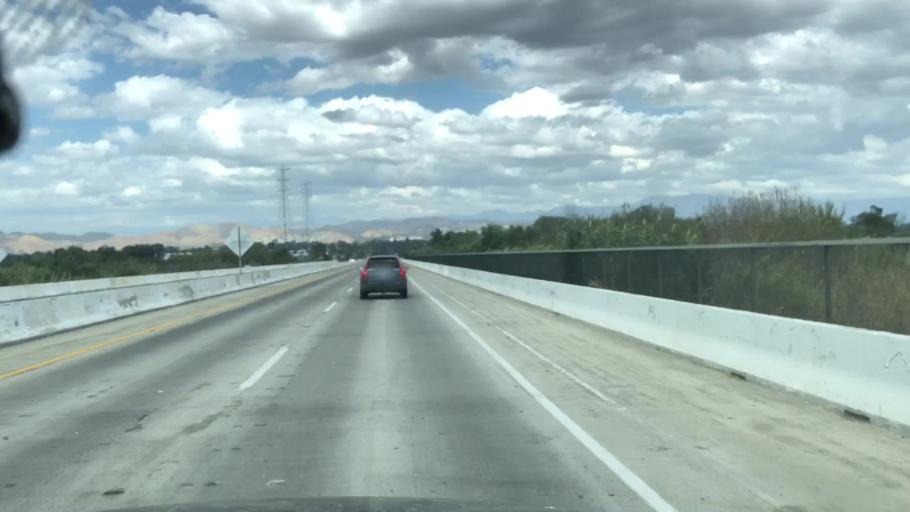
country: US
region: California
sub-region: Ventura County
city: Oxnard Shores
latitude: 34.2338
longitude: -119.2164
